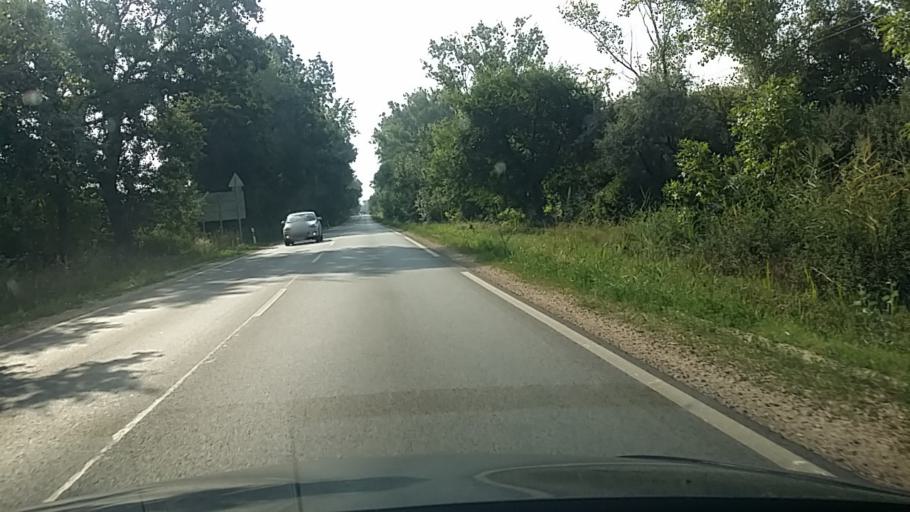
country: HU
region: Bekes
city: Szarvas
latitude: 46.8383
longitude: 20.6293
